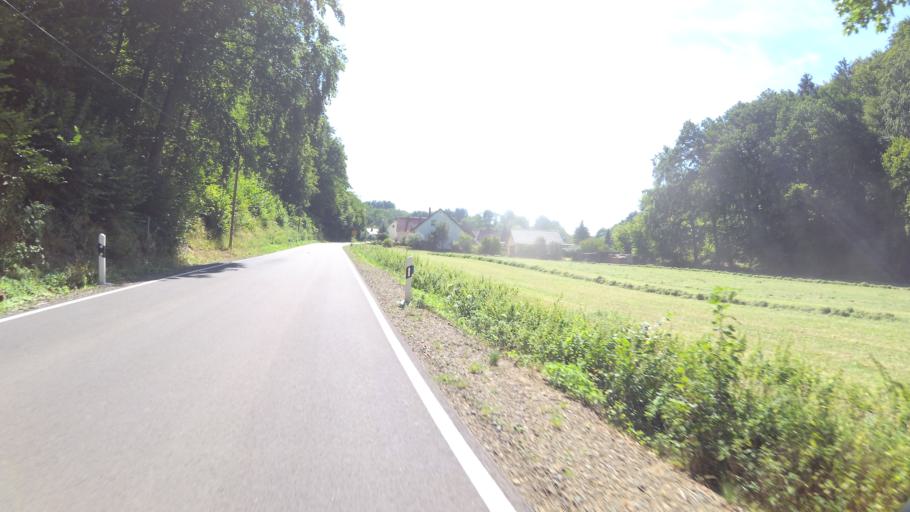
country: DE
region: Rheinland-Pfalz
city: Zweibrucken
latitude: 49.2391
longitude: 7.3157
